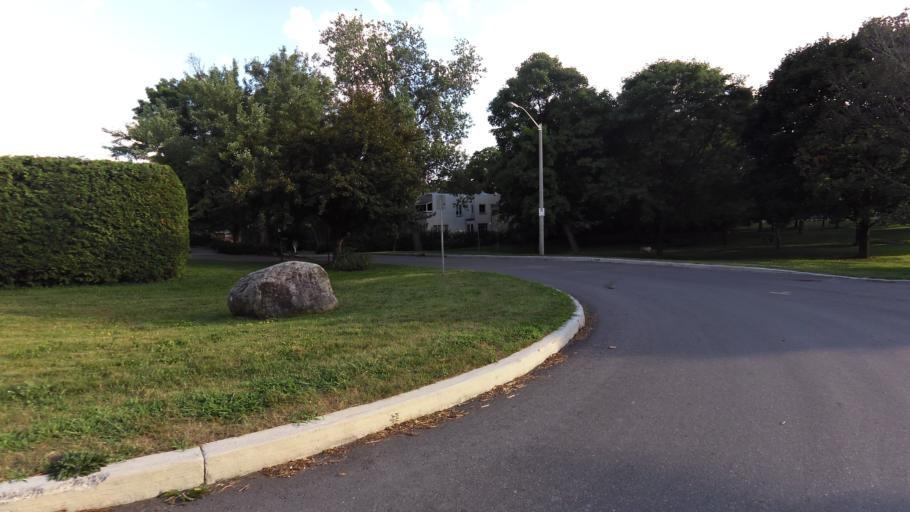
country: CA
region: Ontario
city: Ottawa
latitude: 45.3978
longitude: -75.7181
